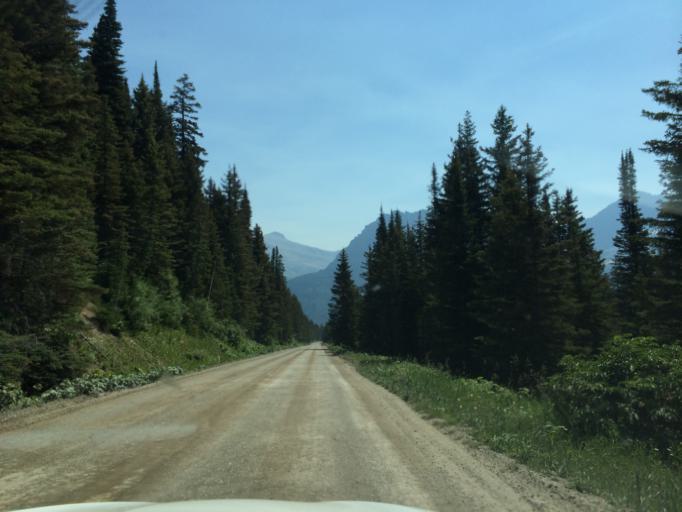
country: US
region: Montana
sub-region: Flathead County
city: Columbia Falls
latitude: 48.6869
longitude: -113.6656
